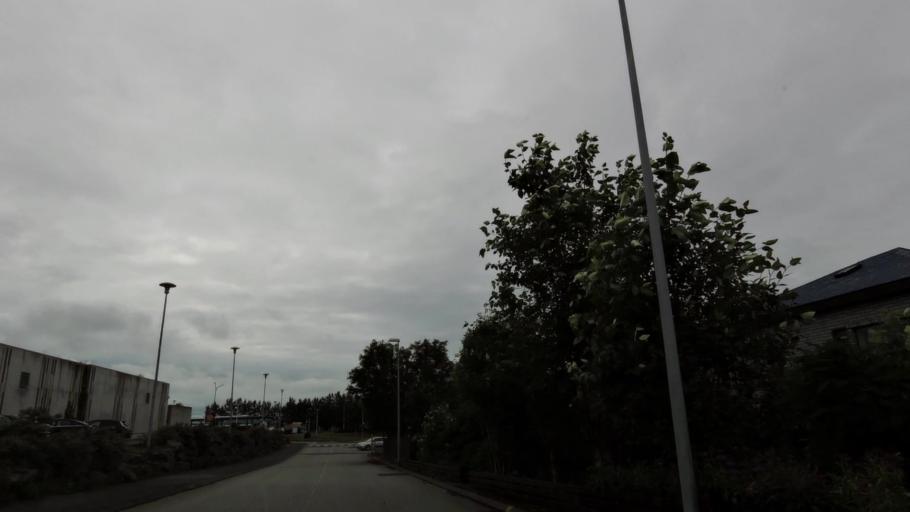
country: IS
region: Capital Region
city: Gardabaer
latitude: 64.0911
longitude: -21.9244
